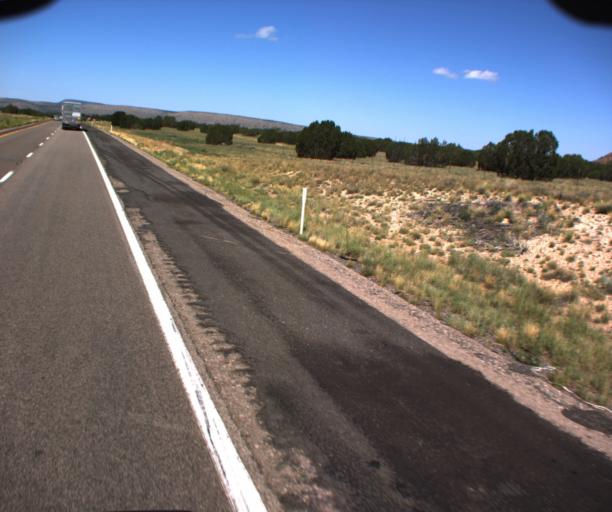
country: US
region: Arizona
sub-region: Mohave County
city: Peach Springs
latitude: 35.3229
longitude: -112.9279
